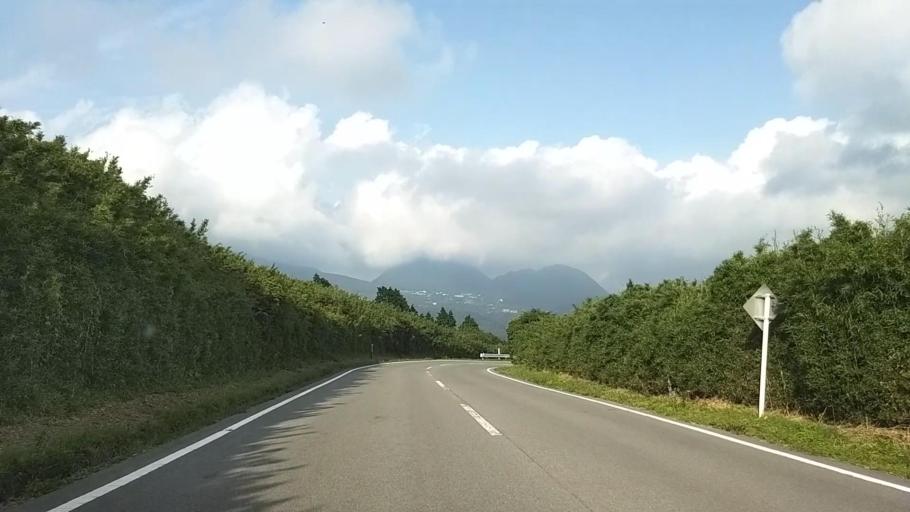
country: JP
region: Kanagawa
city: Hakone
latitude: 35.1934
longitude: 138.9975
